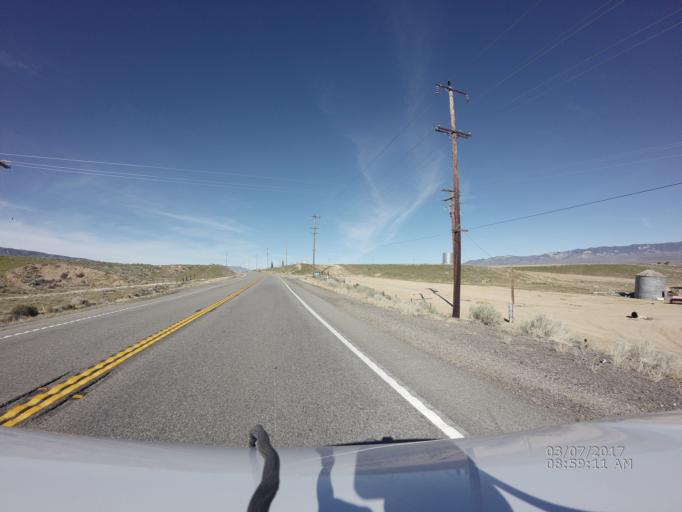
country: US
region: California
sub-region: Los Angeles County
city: Green Valley
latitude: 34.7755
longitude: -118.5699
